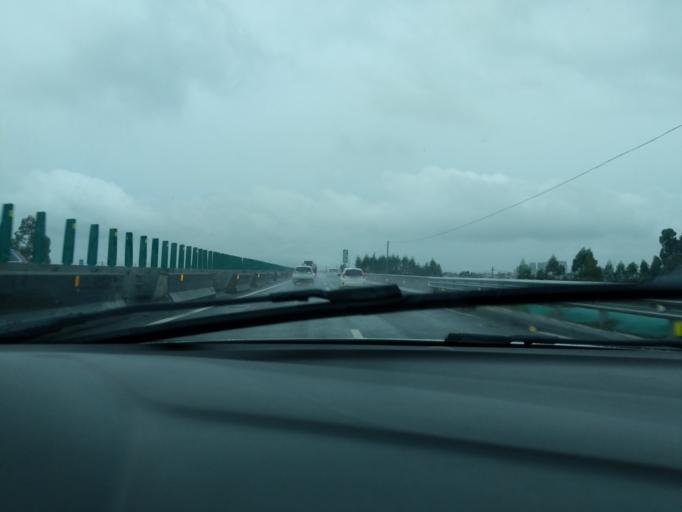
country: CN
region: Guangdong
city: Yueshan
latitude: 22.4634
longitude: 112.7381
